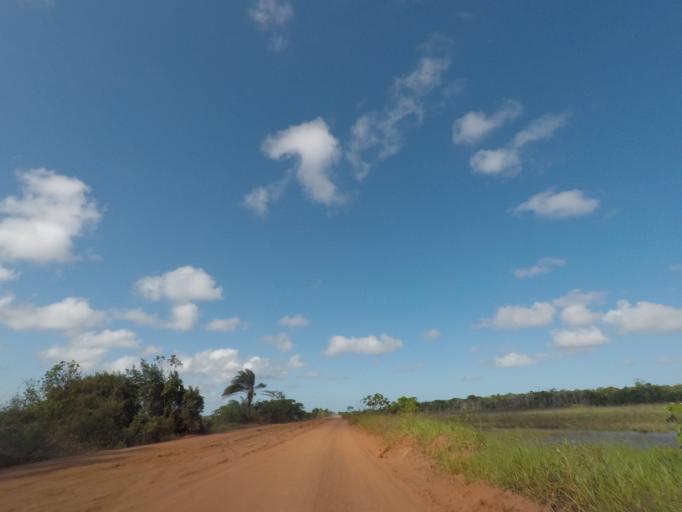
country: BR
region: Bahia
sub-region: Marau
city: Marau
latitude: -14.1669
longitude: -39.0154
